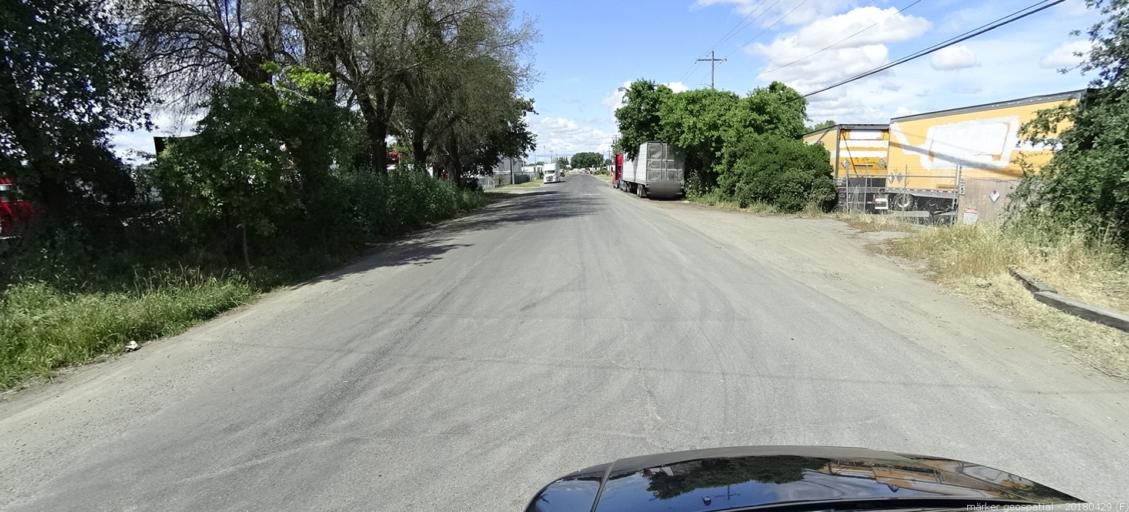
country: US
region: California
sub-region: Yolo County
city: West Sacramento
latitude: 38.5868
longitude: -121.5187
